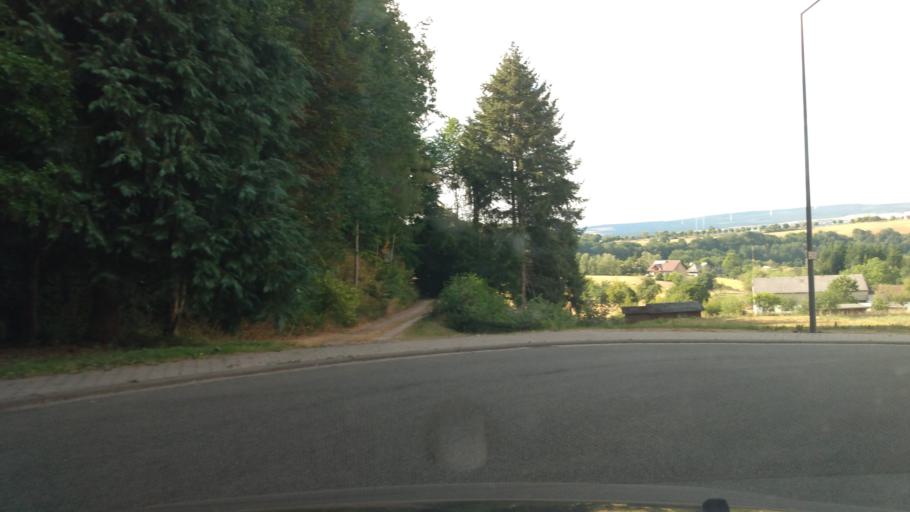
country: DE
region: Rheinland-Pfalz
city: Deuselbach
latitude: 49.7493
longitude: 7.0556
